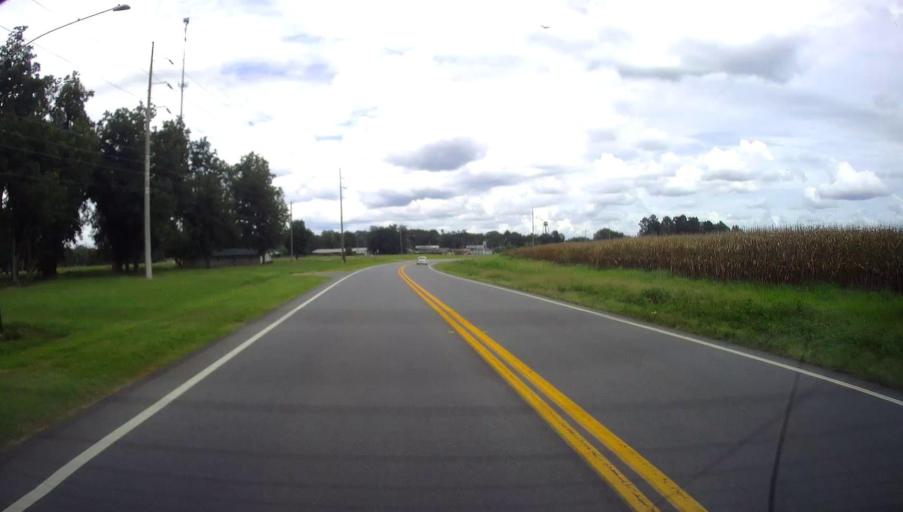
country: US
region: Georgia
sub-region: Macon County
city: Oglethorpe
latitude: 32.2886
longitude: -84.0560
